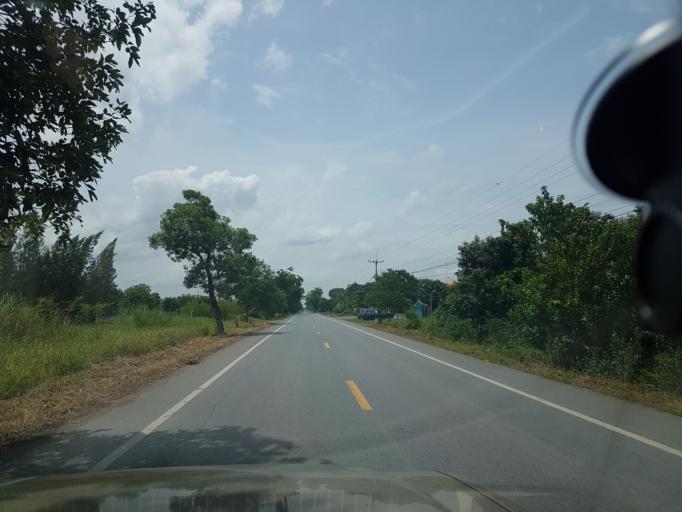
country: TH
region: Pathum Thani
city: Nong Suea
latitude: 14.2104
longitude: 100.8920
